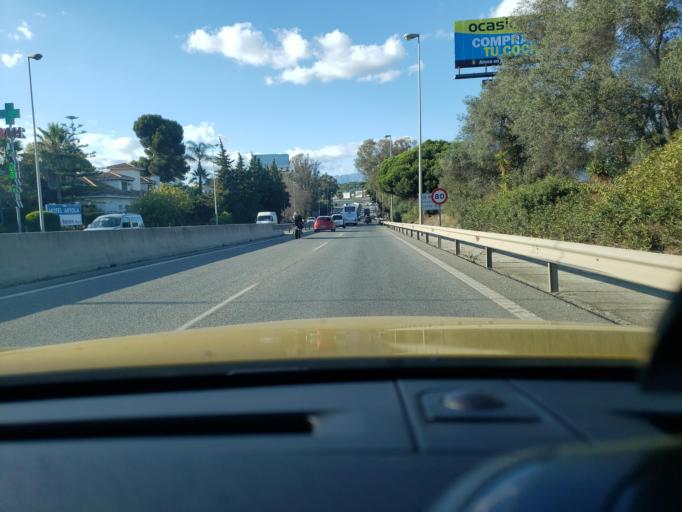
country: ES
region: Andalusia
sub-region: Provincia de Malaga
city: Ojen
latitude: 36.4906
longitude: -4.7475
